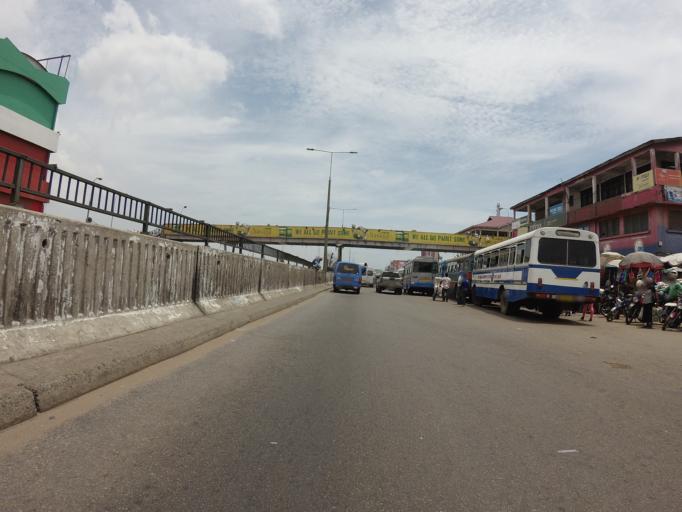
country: GH
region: Greater Accra
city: Accra
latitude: 5.5655
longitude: -0.2363
